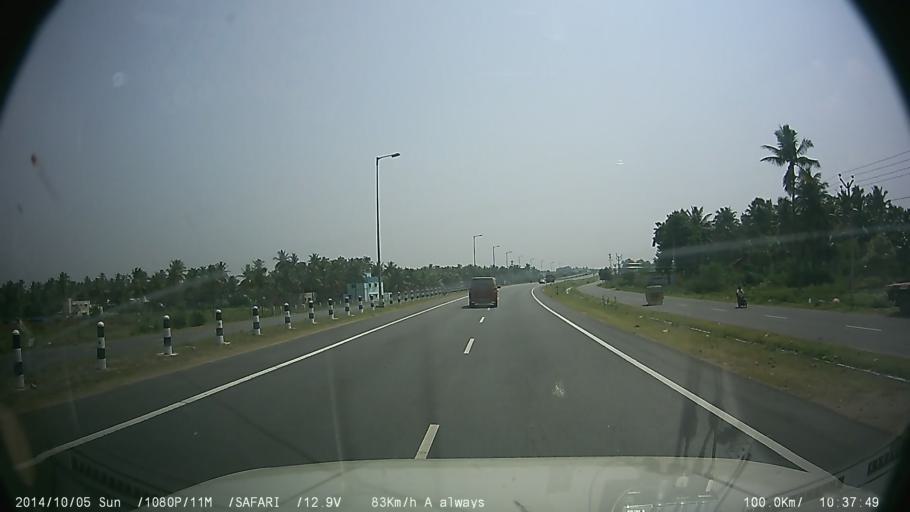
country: IN
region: Tamil Nadu
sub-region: Salem
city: Salem
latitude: 11.6636
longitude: 78.2332
